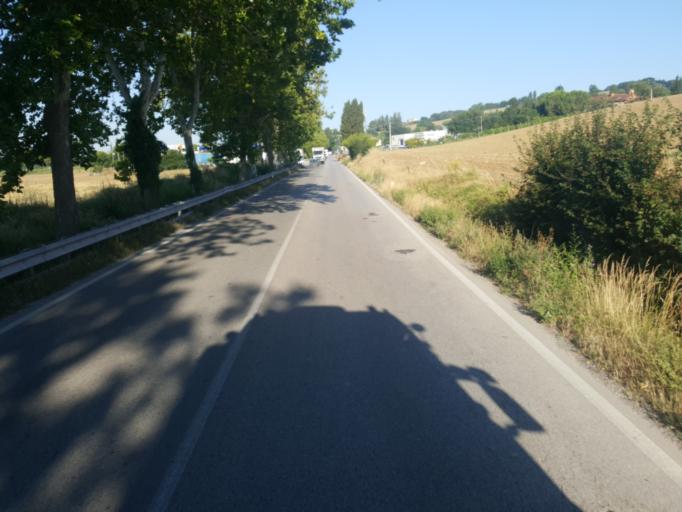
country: IT
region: The Marches
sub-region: Provincia di Pesaro e Urbino
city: Borgo Santa Maria
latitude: 43.8806
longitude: 12.8223
